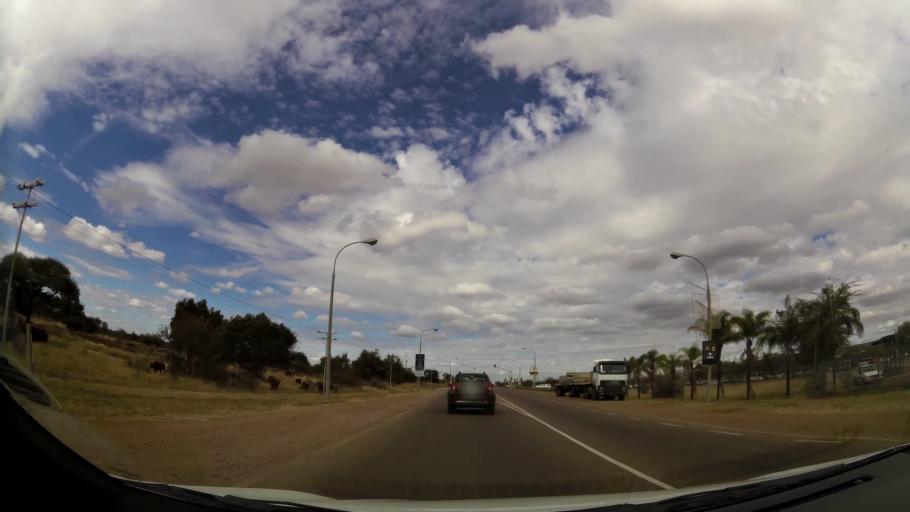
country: ZA
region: Limpopo
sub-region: Waterberg District Municipality
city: Bela-Bela
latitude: -24.8941
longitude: 28.2958
